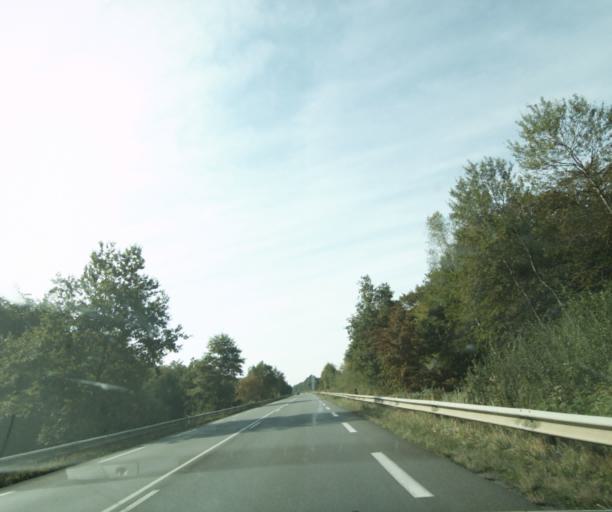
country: FR
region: Bourgogne
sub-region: Departement de Saone-et-Loire
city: Palinges
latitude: 46.5342
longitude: 4.1688
